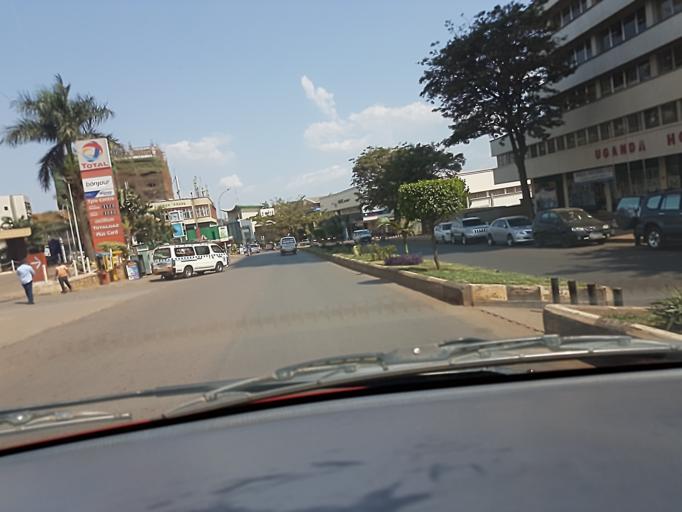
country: UG
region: Central Region
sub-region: Kampala District
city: Kampala
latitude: 0.3126
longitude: 32.5843
